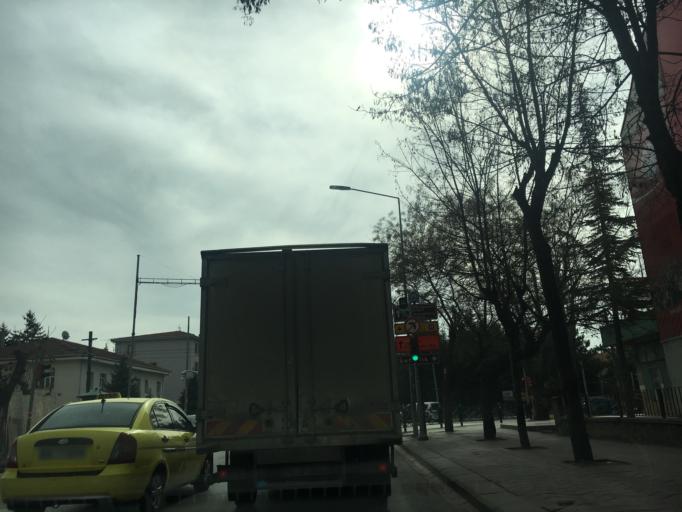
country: TR
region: Eskisehir
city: Eskisehir
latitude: 39.7712
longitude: 30.5153
